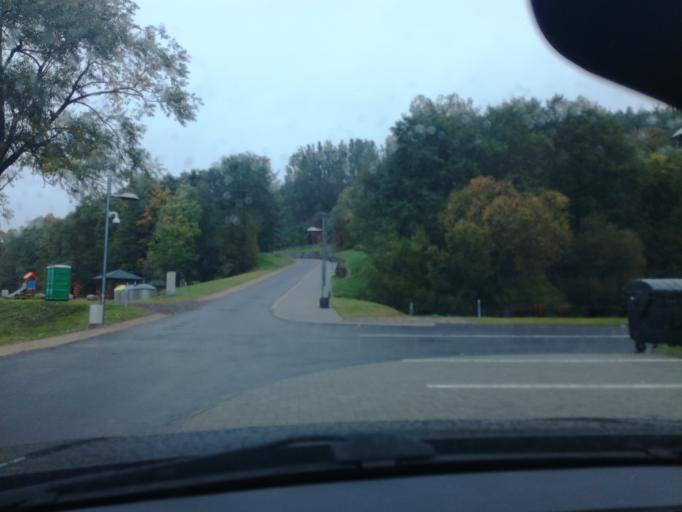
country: LT
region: Alytaus apskritis
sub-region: Alytus
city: Alytus
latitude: 54.3964
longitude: 24.0782
